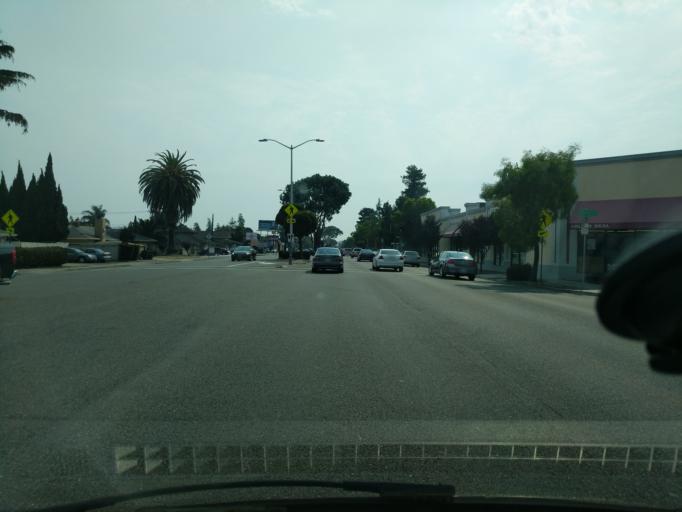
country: US
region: California
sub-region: Alameda County
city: Hayward
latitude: 37.6607
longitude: -122.0853
